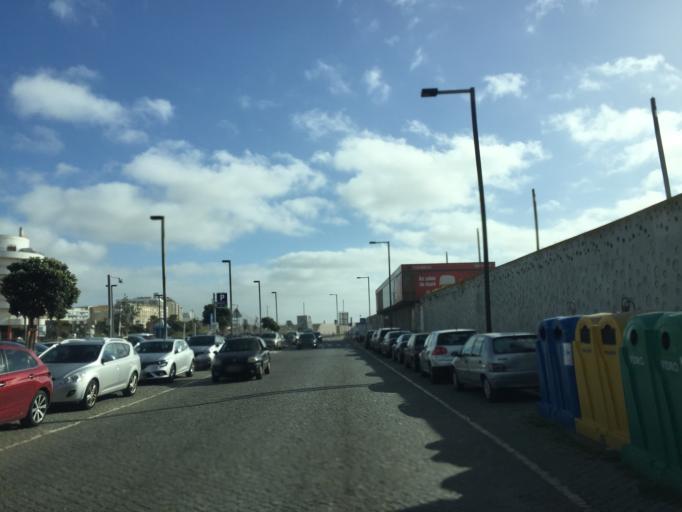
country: PT
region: Setubal
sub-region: Almada
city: Costa de Caparica
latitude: 38.6458
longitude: -9.2418
